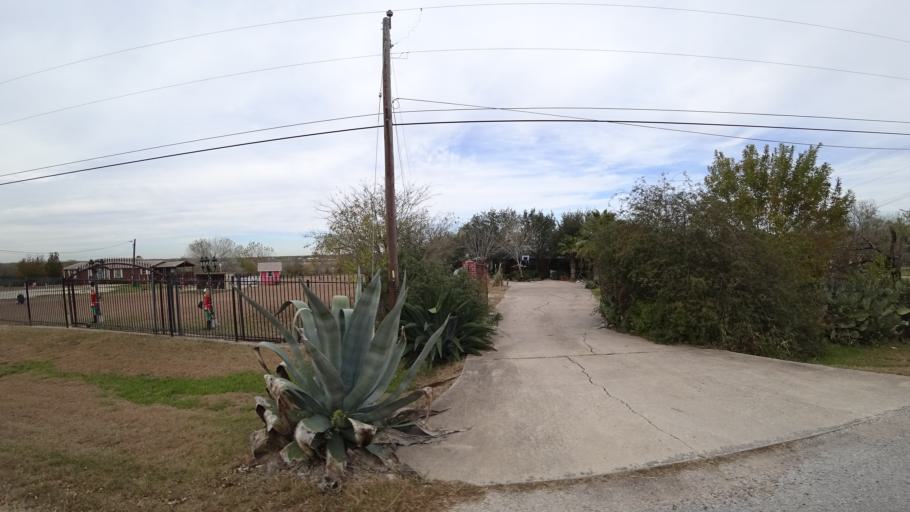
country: US
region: Texas
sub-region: Travis County
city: Garfield
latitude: 30.1168
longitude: -97.5826
